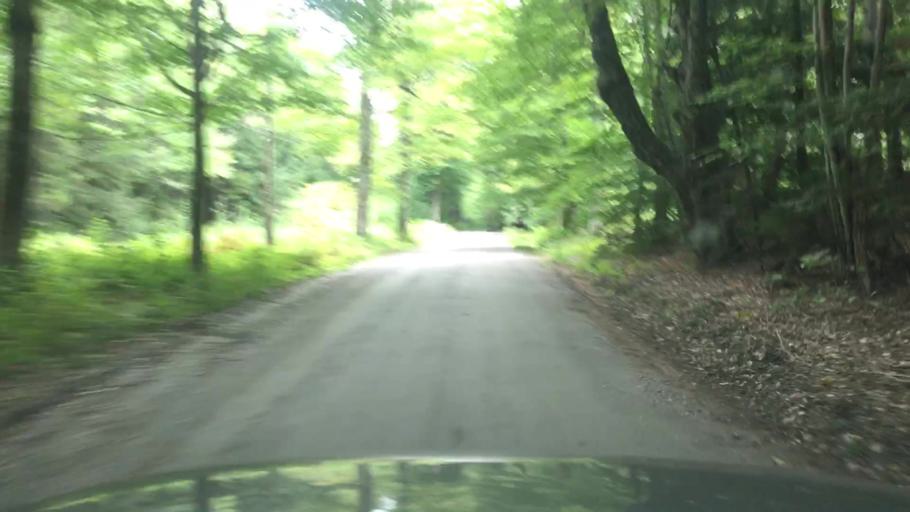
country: US
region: Vermont
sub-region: Windham County
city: Dover
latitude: 42.8392
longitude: -72.7677
